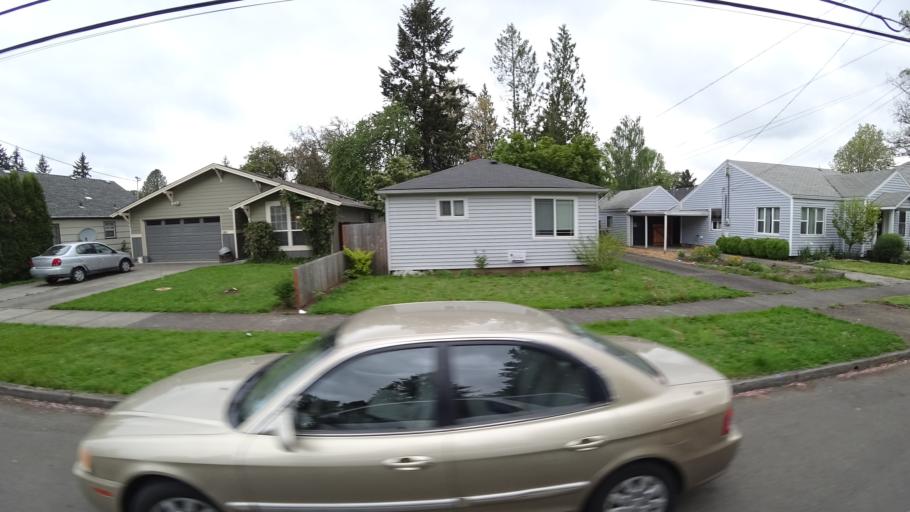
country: US
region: Oregon
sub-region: Washington County
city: Hillsboro
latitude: 45.5284
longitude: -122.9885
